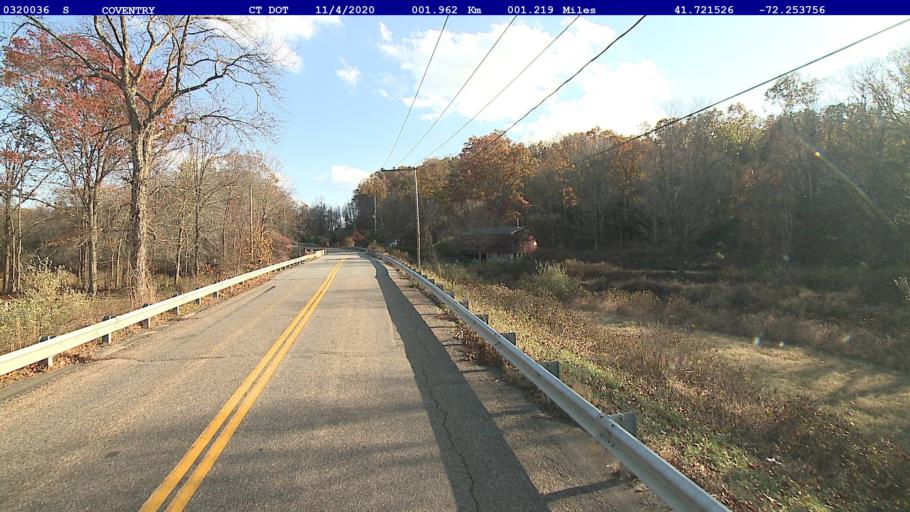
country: US
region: Connecticut
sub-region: Windham County
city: Willimantic
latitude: 41.7215
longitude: -72.2538
